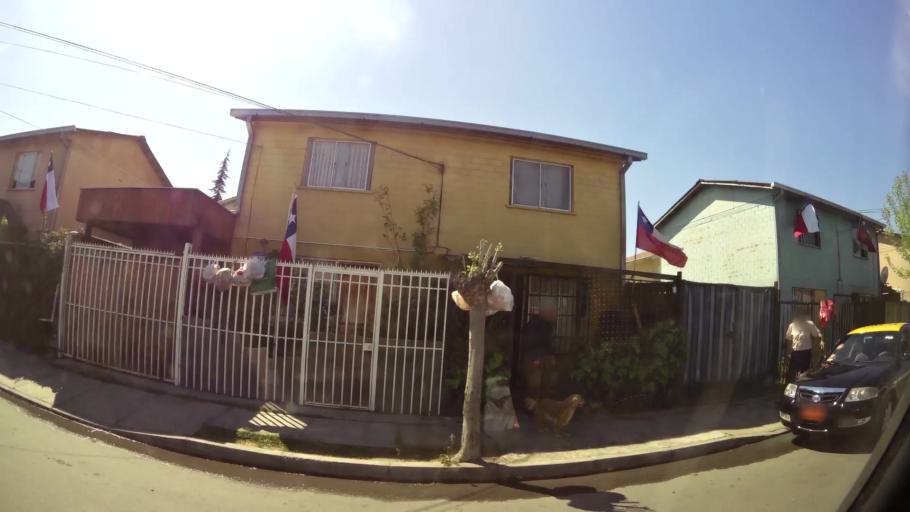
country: CL
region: Santiago Metropolitan
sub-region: Provincia de Talagante
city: Penaflor
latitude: -33.6075
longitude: -70.8799
